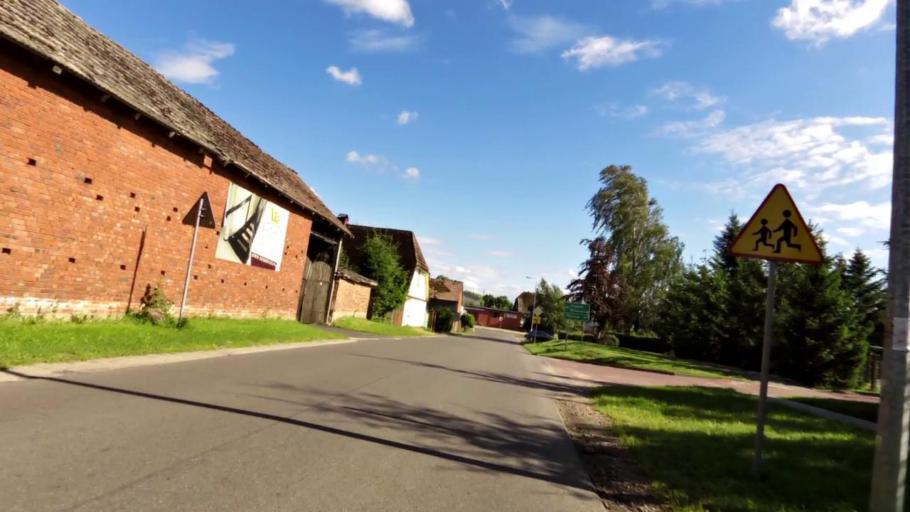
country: PL
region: West Pomeranian Voivodeship
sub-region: Powiat slawienski
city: Slawno
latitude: 54.4353
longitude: 16.7331
